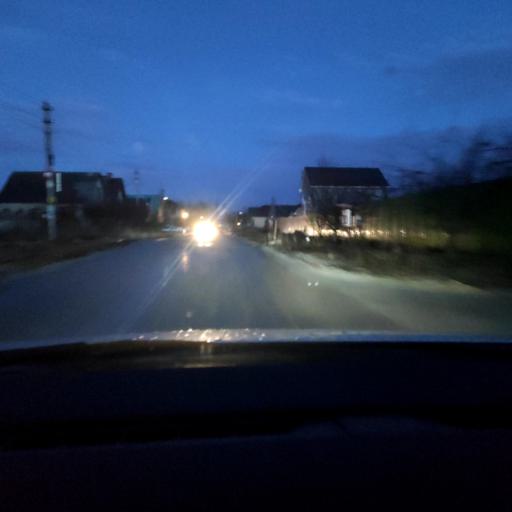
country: RU
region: Voronezj
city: Semiluki
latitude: 51.7123
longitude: 39.0219
